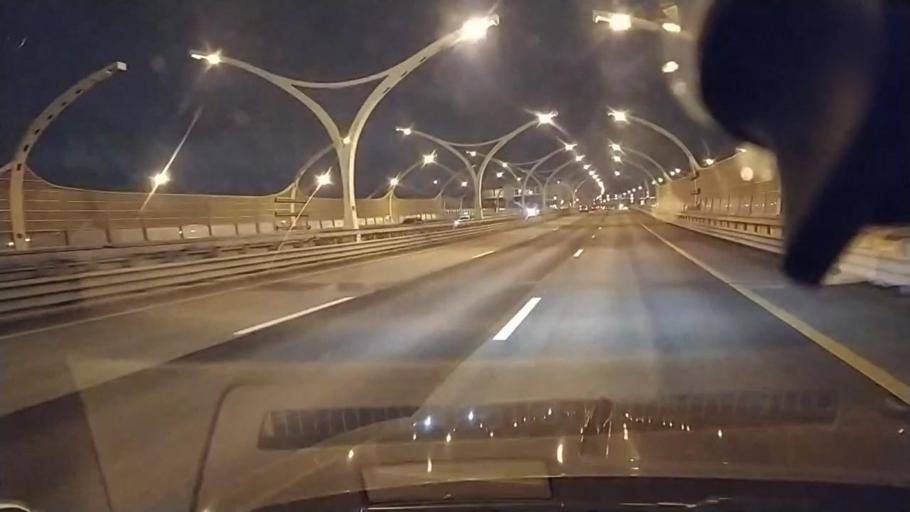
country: RU
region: St.-Petersburg
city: Staraya Derevnya
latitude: 60.0004
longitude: 30.2320
